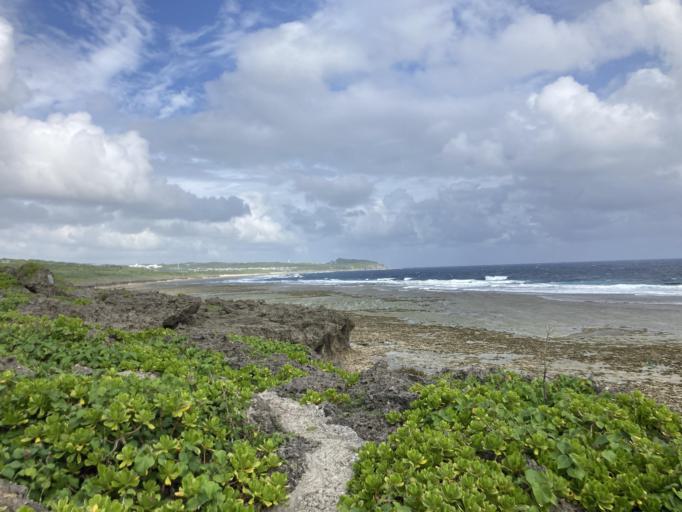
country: JP
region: Okinawa
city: Itoman
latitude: 26.0775
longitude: 127.6825
